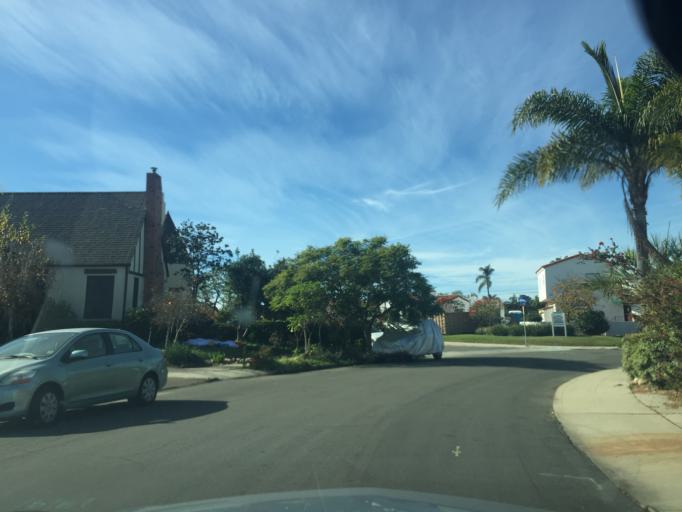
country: US
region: California
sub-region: San Diego County
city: Lemon Grove
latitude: 32.7664
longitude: -117.1004
